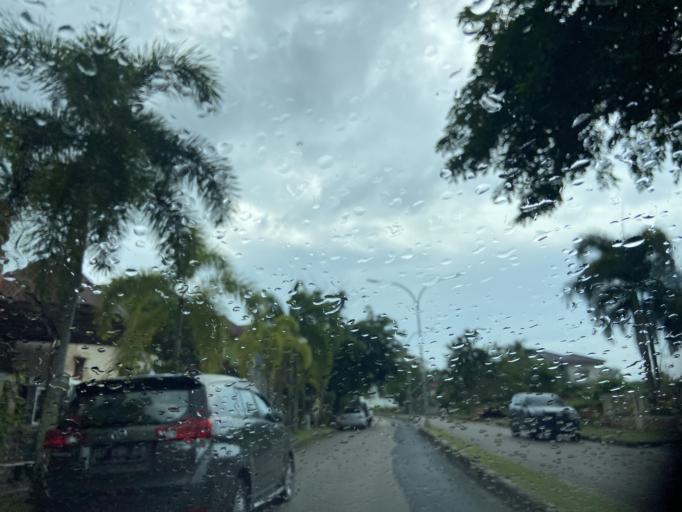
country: SG
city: Singapore
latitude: 1.1052
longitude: 104.0255
